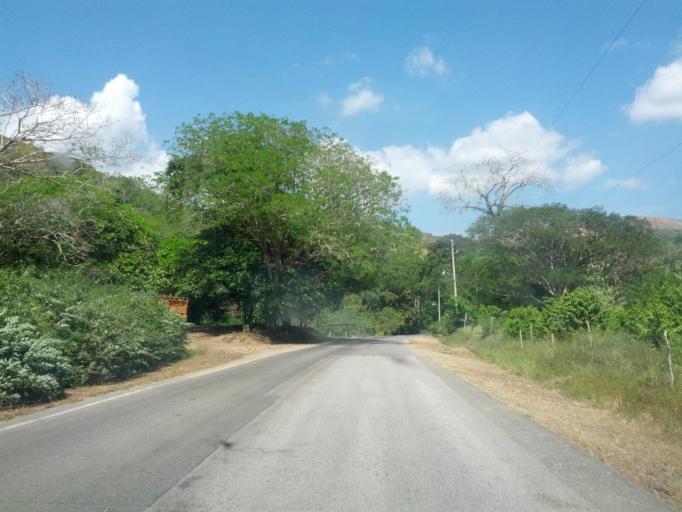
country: CR
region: Puntarenas
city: Buenos Aires
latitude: 8.9641
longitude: -83.3079
